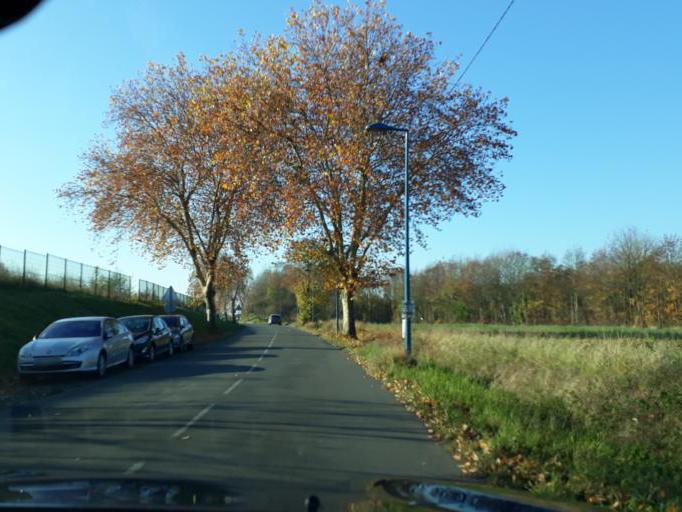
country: FR
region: Nord-Pas-de-Calais
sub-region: Departement du Nord
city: Dechy
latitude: 50.3492
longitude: 3.1198
